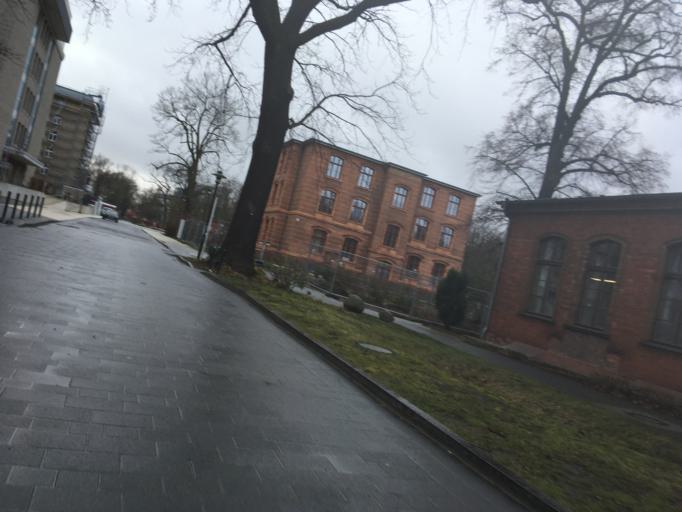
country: DE
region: Berlin
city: Prenzlauer Berg Bezirk
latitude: 52.5264
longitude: 13.4379
